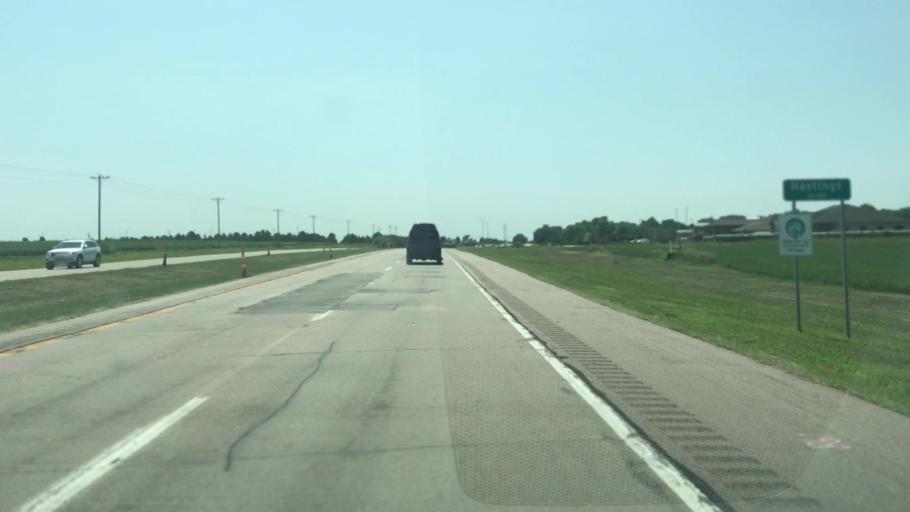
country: US
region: Nebraska
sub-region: Adams County
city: Hastings
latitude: 40.6447
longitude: -98.3823
